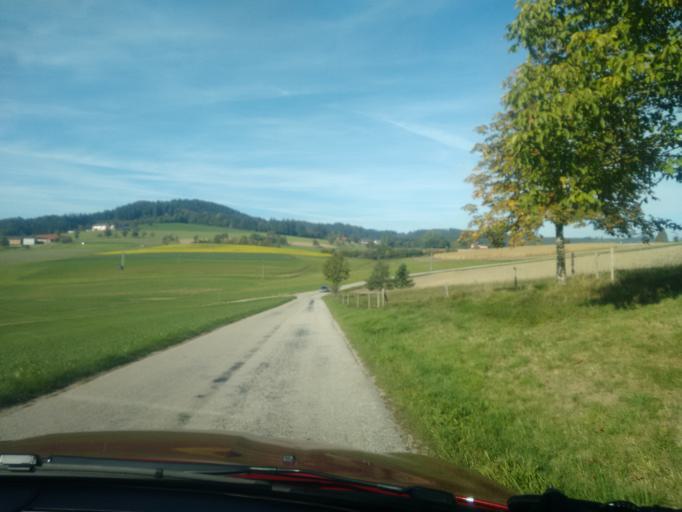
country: AT
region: Upper Austria
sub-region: Politischer Bezirk Vocklabruck
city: Manning
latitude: 48.0745
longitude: 13.6426
